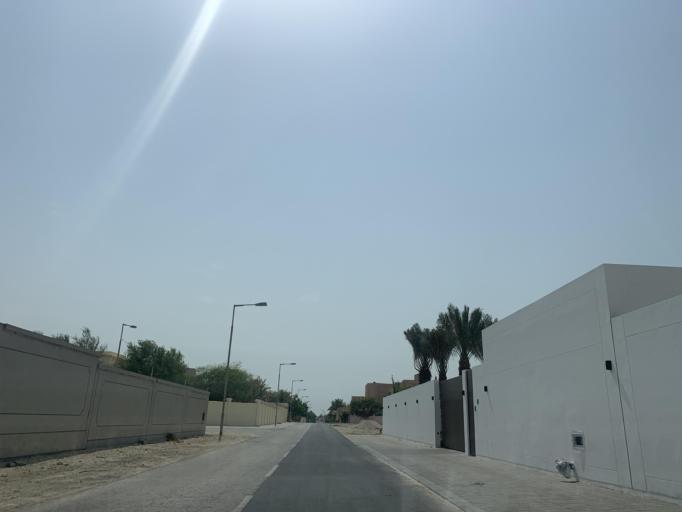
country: BH
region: Central Governorate
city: Madinat Hamad
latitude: 26.1649
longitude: 50.4827
